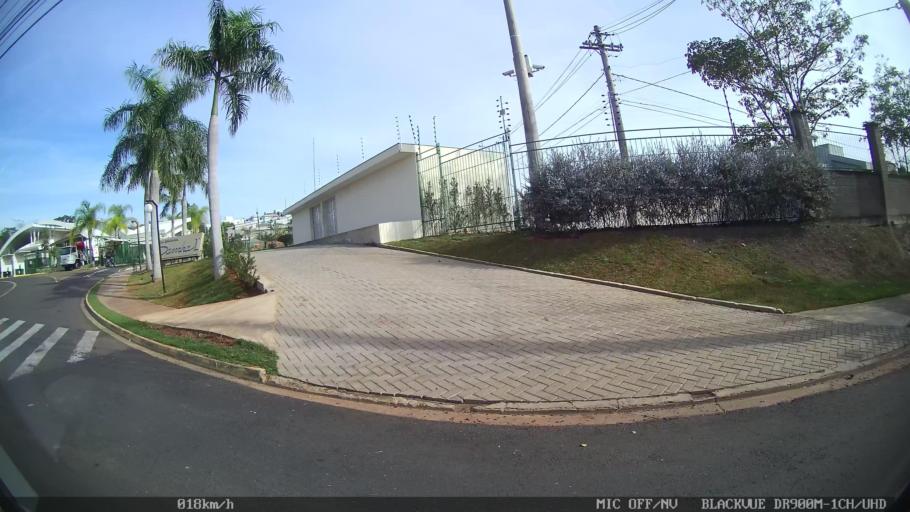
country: BR
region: Sao Paulo
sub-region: Piracicaba
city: Piracicaba
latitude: -22.7042
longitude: -47.6766
